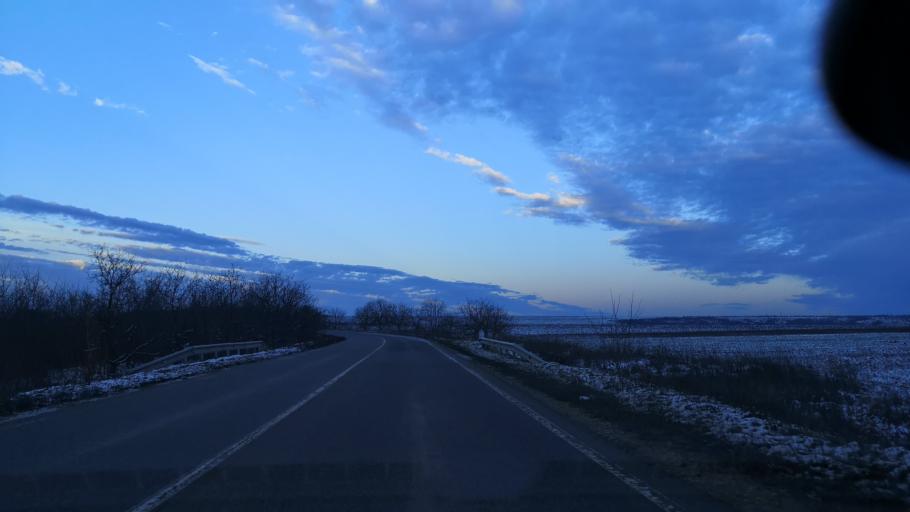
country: MD
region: Orhei
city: Orhei
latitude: 47.5569
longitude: 28.7976
